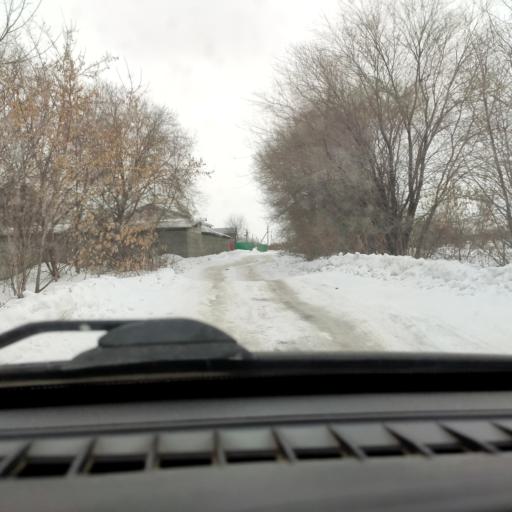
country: RU
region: Samara
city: Tol'yatti
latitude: 53.5680
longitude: 49.4721
